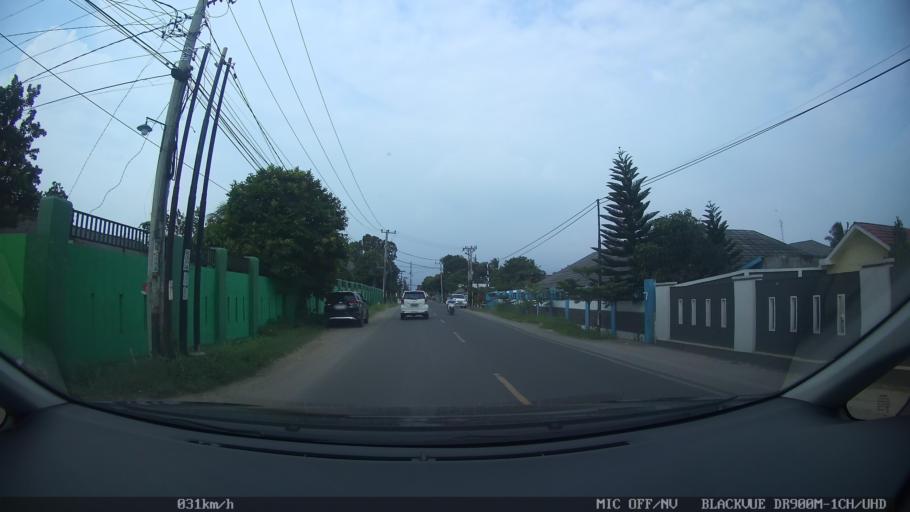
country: ID
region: Lampung
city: Kedaton
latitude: -5.3659
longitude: 105.2189
